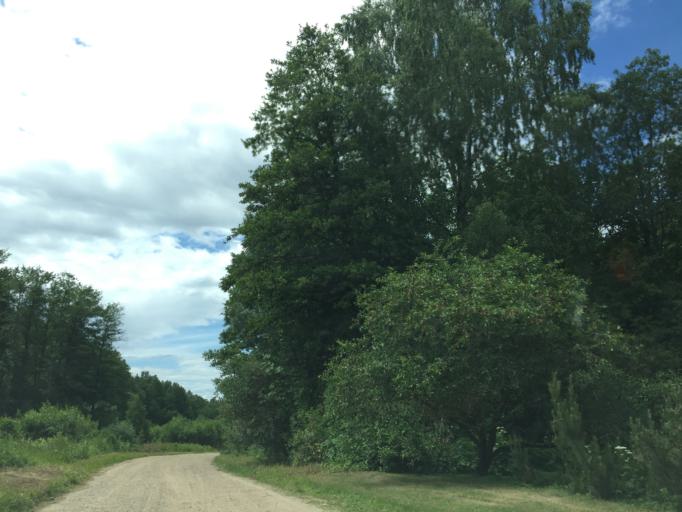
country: LV
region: Saulkrastu
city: Saulkrasti
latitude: 57.4164
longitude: 24.4194
